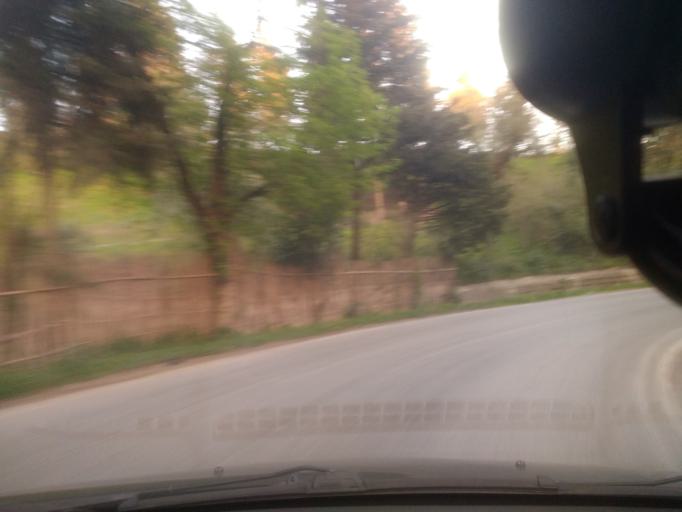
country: DZ
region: Boumerdes
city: Makouda
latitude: 36.7815
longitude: 4.0687
